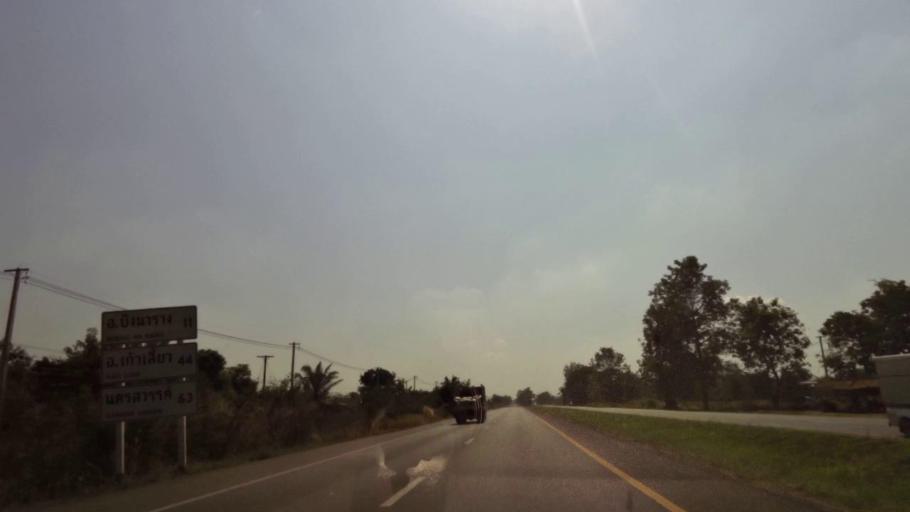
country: TH
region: Phichit
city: Bueng Na Rang
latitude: 16.2615
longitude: 100.1261
